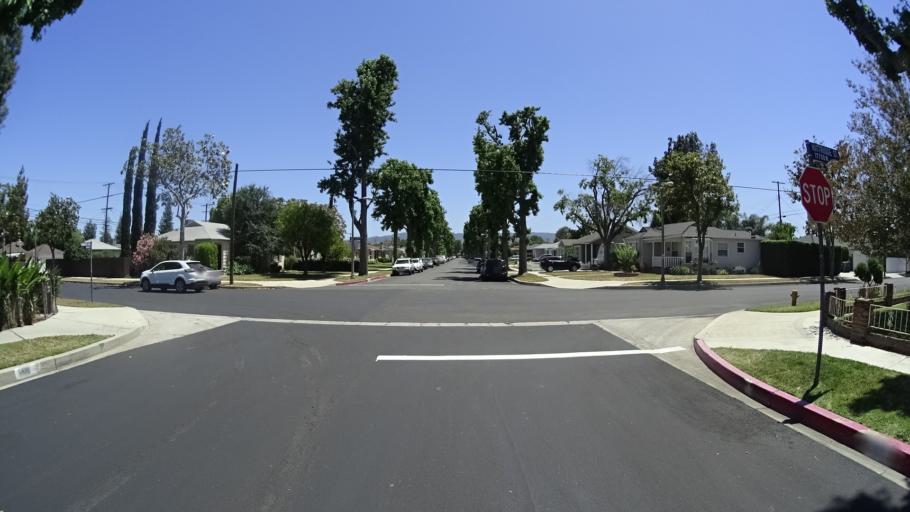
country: US
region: California
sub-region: Los Angeles County
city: Northridge
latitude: 34.1905
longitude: -118.5197
